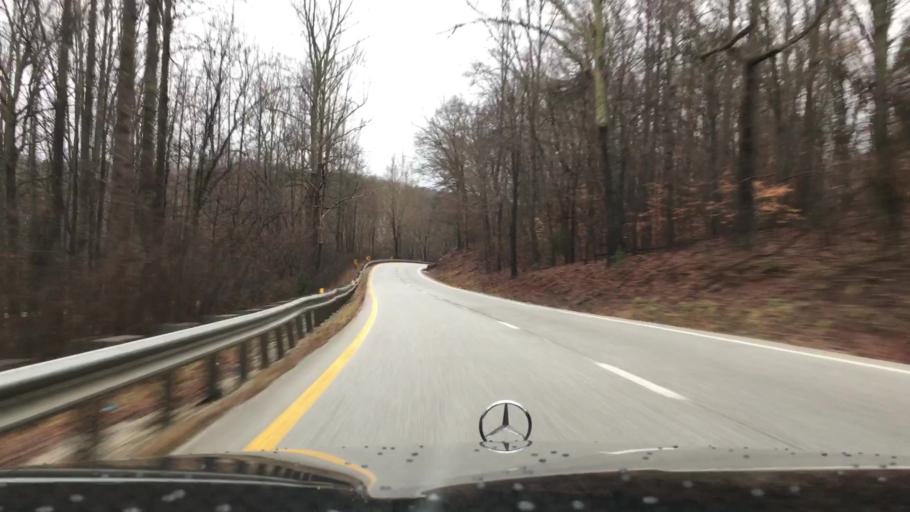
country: US
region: Virginia
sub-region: Nelson County
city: Nellysford
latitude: 37.8256
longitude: -78.8391
